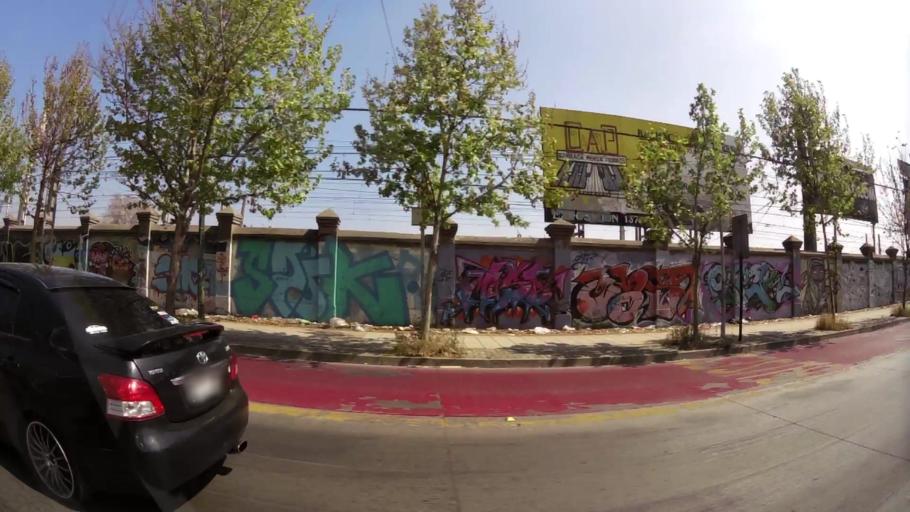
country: CL
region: Santiago Metropolitan
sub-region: Provincia de Santiago
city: Santiago
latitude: -33.4584
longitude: -70.6784
